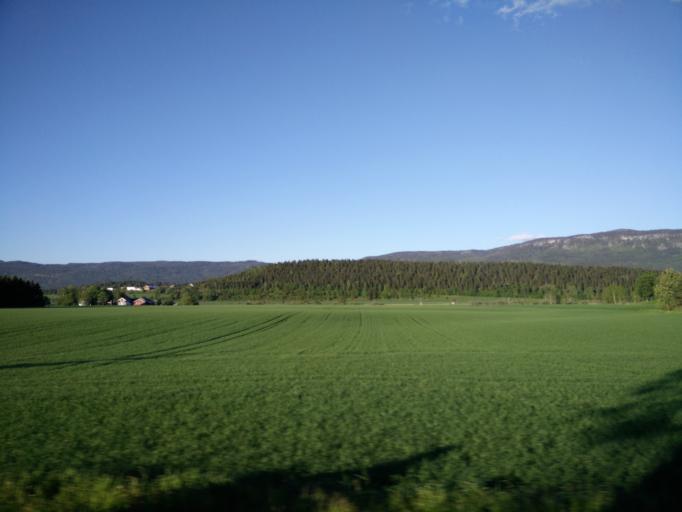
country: NO
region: Buskerud
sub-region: Hole
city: Vik
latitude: 60.1058
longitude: 10.2875
